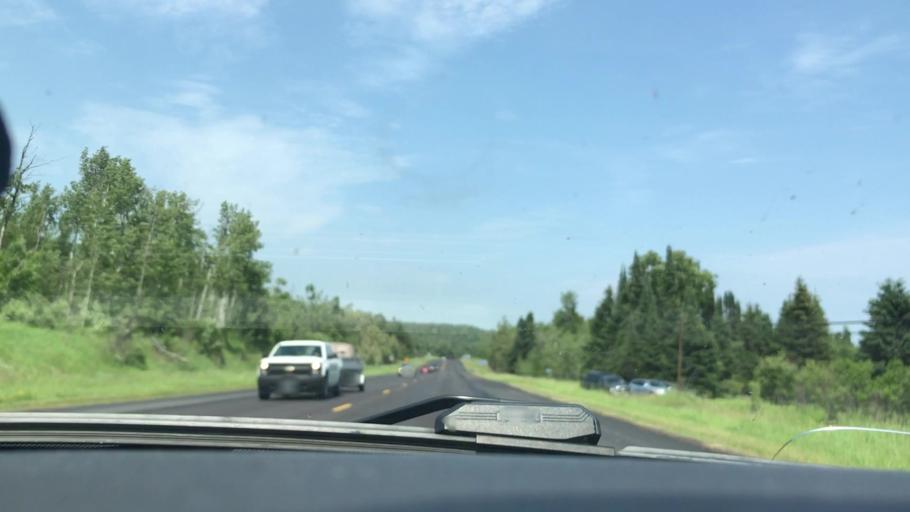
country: US
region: Minnesota
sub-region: Lake County
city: Silver Bay
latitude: 47.3294
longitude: -91.2090
